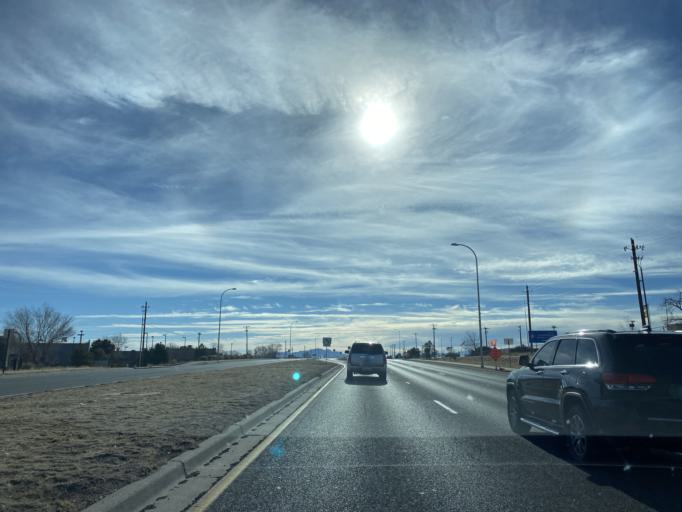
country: US
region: New Mexico
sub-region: Santa Fe County
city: Agua Fria
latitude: 35.6260
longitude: -106.0255
